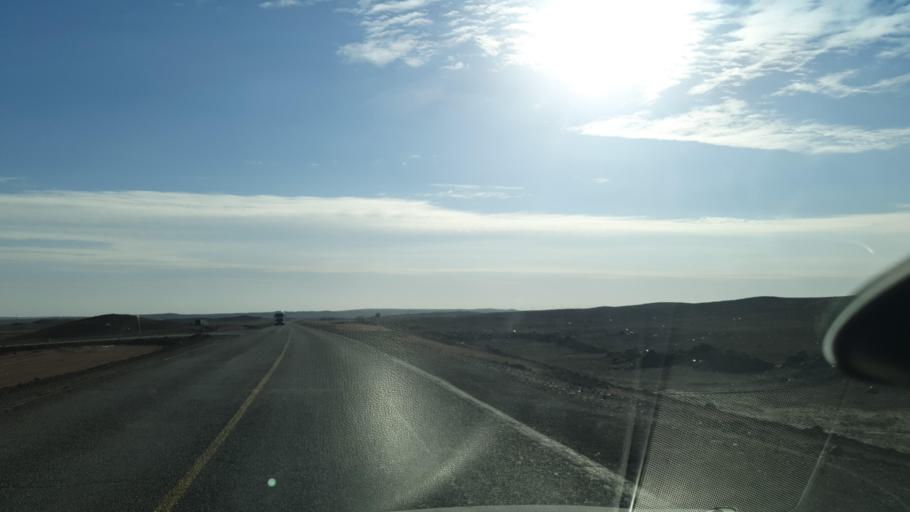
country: KZ
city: Priozersk
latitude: 45.7951
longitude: 73.3901
